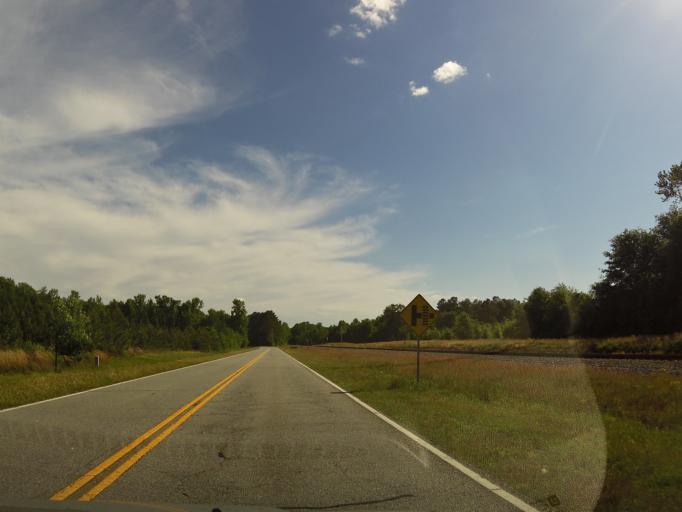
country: US
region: South Carolina
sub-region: Bamberg County
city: Denmark
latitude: 33.1588
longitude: -81.1924
